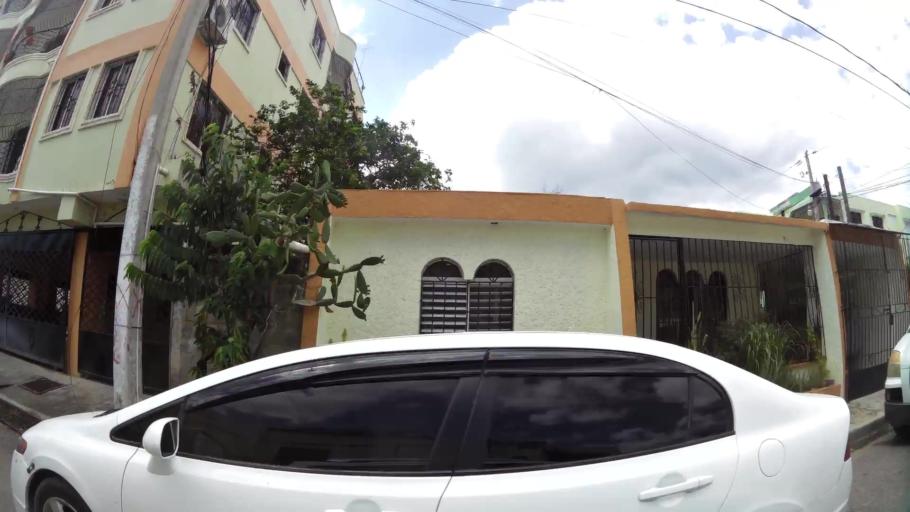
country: DO
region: San Cristobal
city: San Cristobal
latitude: 18.4131
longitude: -70.0979
